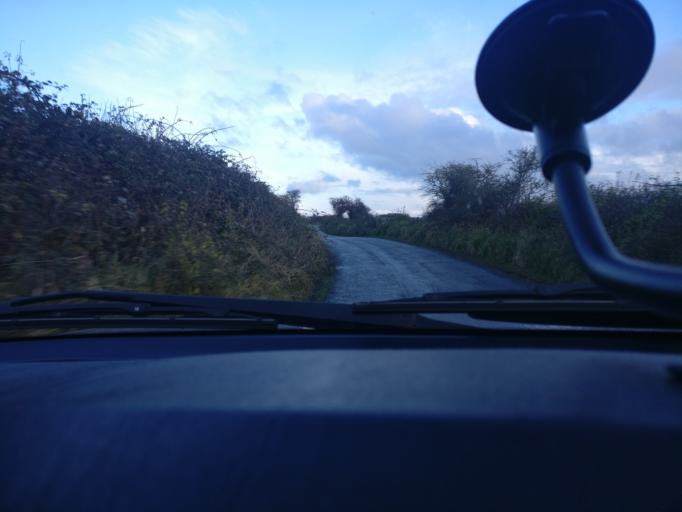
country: IE
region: Connaught
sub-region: County Galway
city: Athenry
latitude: 53.1975
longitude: -8.6895
